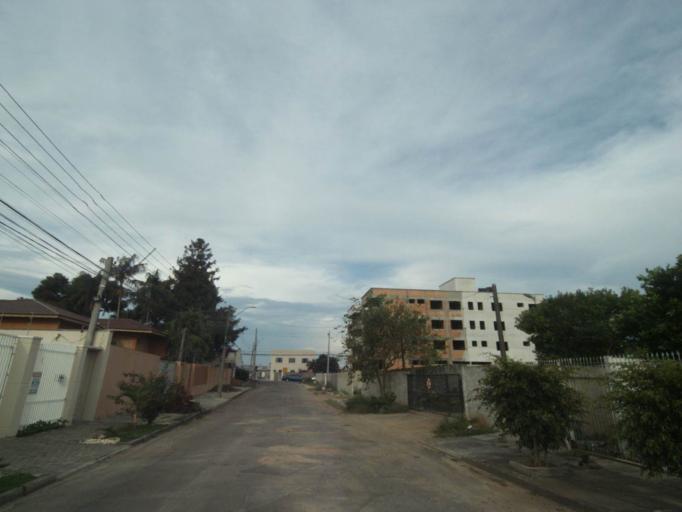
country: BR
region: Parana
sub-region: Pinhais
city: Pinhais
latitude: -25.4645
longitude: -49.2162
